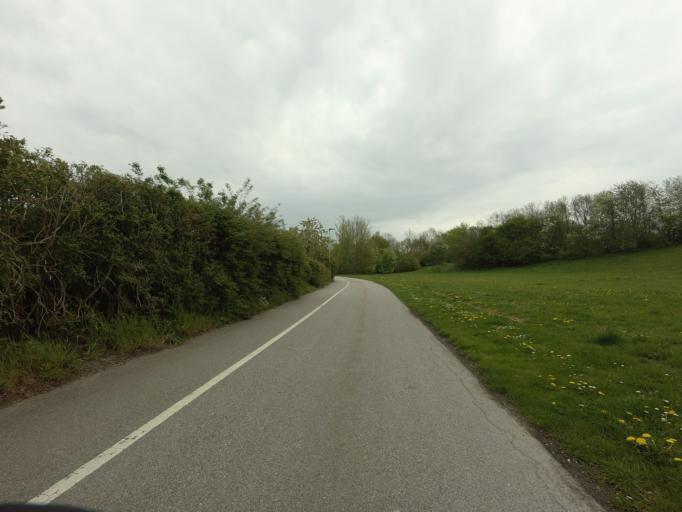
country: SE
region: Skane
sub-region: Malmo
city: Tygelsjo
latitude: 55.5530
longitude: 13.0166
